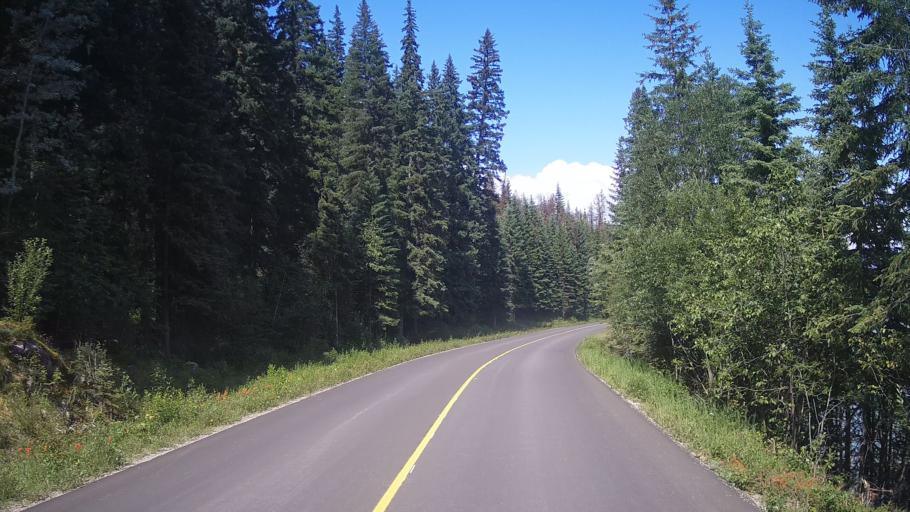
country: CA
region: Alberta
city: Jasper Park Lodge
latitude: 52.7418
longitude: -117.9651
